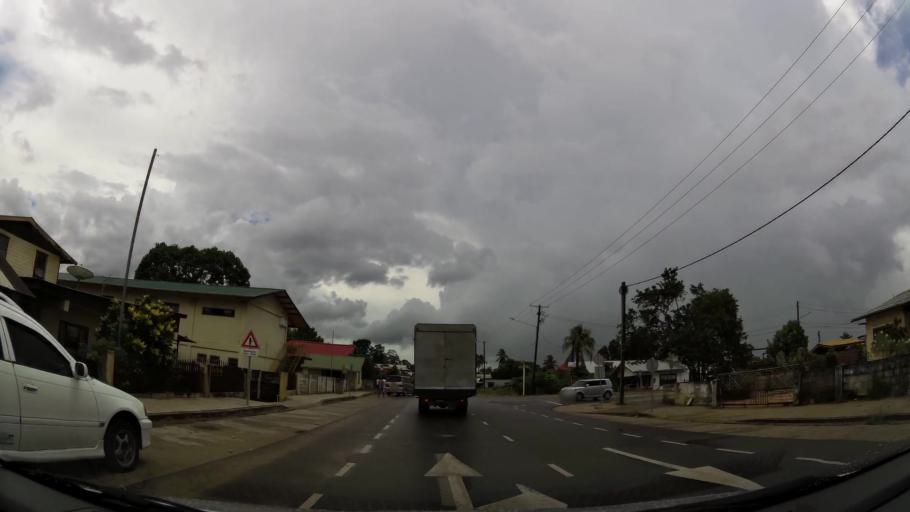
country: SR
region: Paramaribo
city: Paramaribo
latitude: 5.7900
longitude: -55.1916
